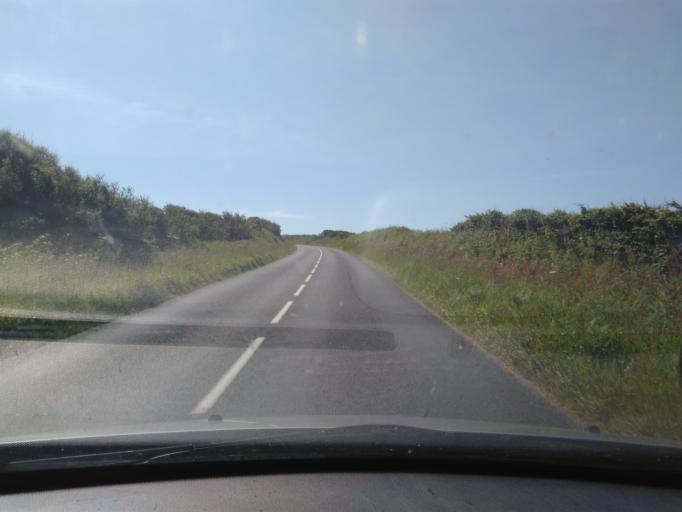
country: FR
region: Lower Normandy
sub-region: Departement de la Manche
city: Beaumont-Hague
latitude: 49.6989
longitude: -1.9261
